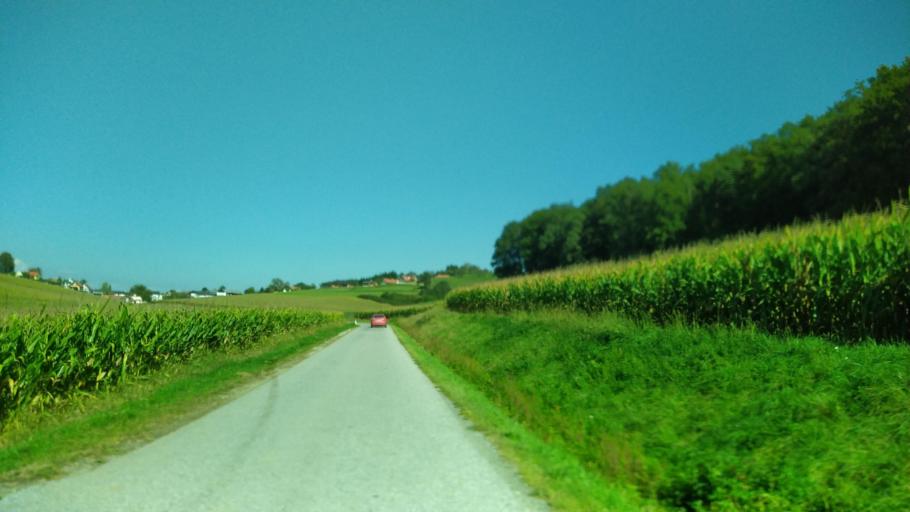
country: AT
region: Styria
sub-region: Politischer Bezirk Deutschlandsberg
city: Wettmannstatten
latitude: 46.8173
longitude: 15.3775
